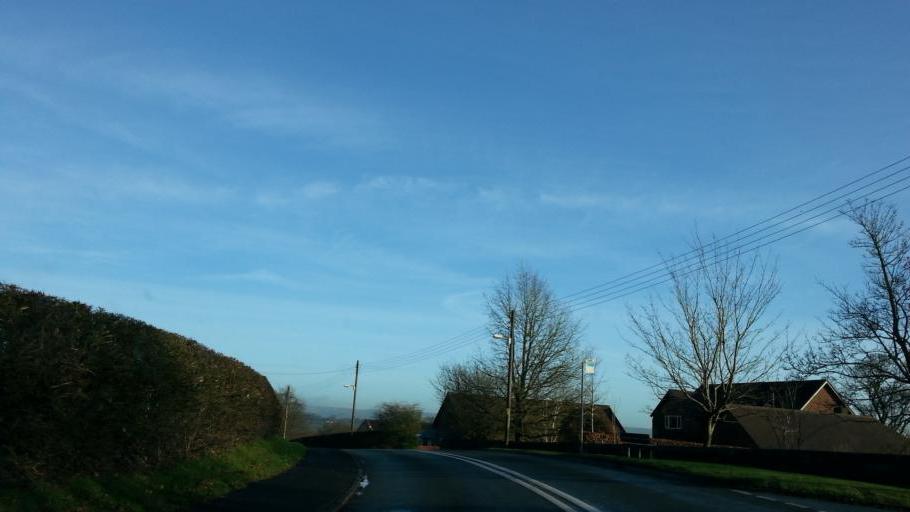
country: GB
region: England
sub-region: Staffordshire
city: Biddulph
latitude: 53.0774
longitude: -2.1259
